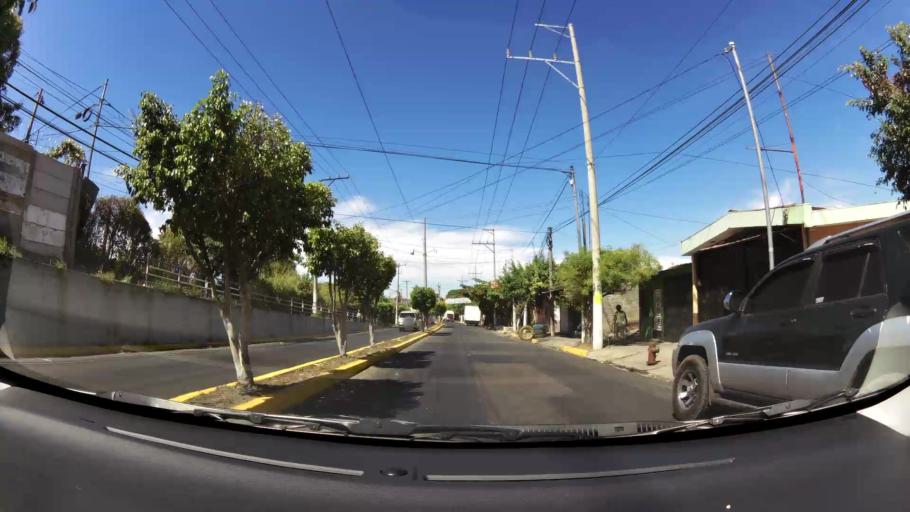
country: SV
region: La Libertad
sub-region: Distrito de Quezaltepeque
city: Quezaltepeque
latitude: 13.8296
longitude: -89.2668
